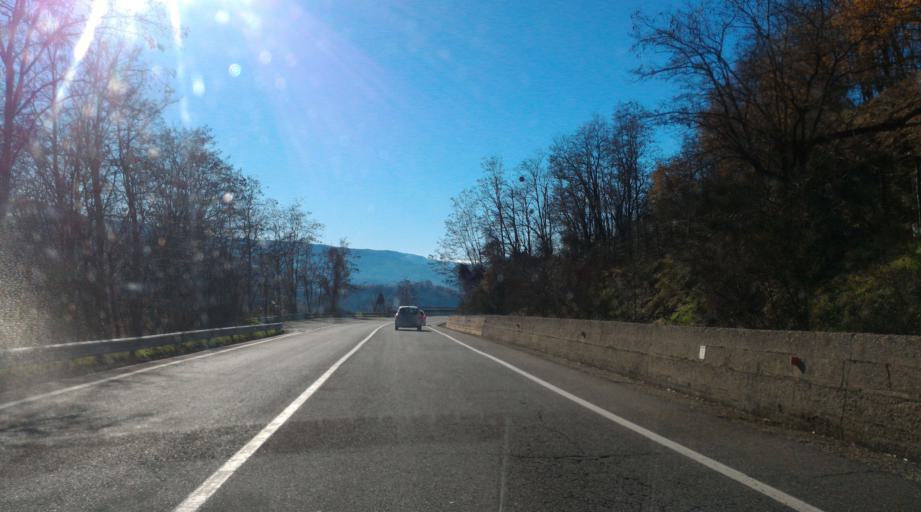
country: IT
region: Calabria
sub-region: Provincia di Cosenza
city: Spezzano della Sila
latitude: 39.3004
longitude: 16.3559
